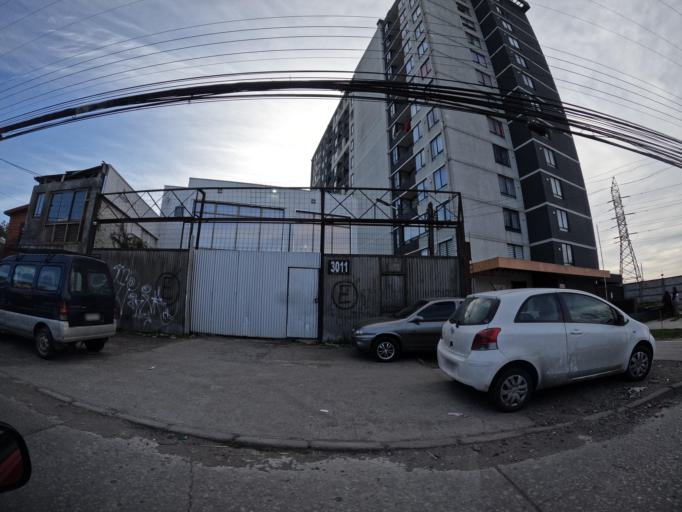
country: CL
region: Biobio
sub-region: Provincia de Concepcion
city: Concepcion
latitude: -36.8039
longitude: -73.0303
